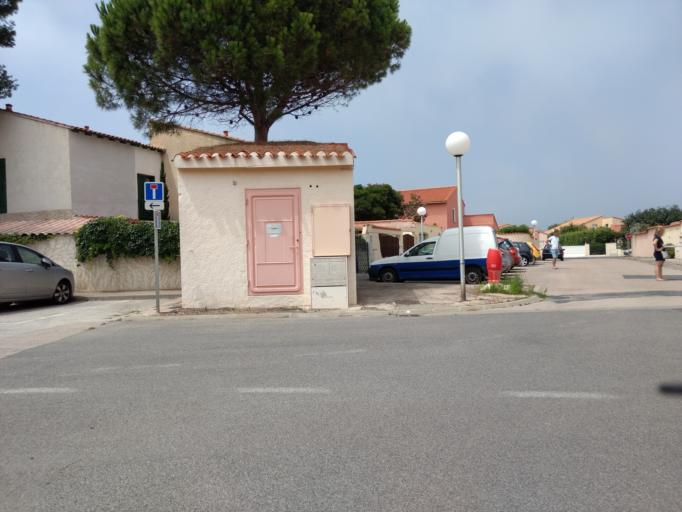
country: FR
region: Languedoc-Roussillon
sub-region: Departement des Pyrenees-Orientales
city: Le Barcares
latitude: 42.7926
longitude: 3.0305
